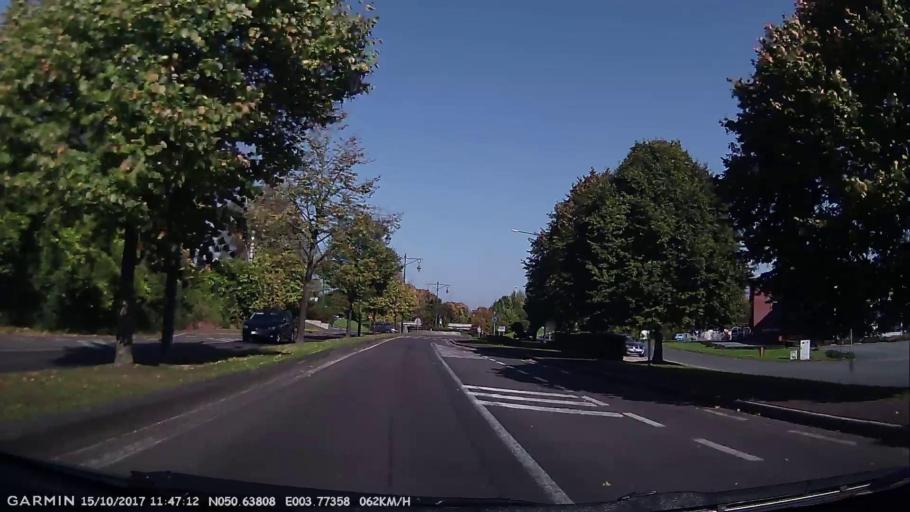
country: BE
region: Wallonia
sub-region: Province du Hainaut
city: Ath
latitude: 50.6383
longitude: 3.7736
